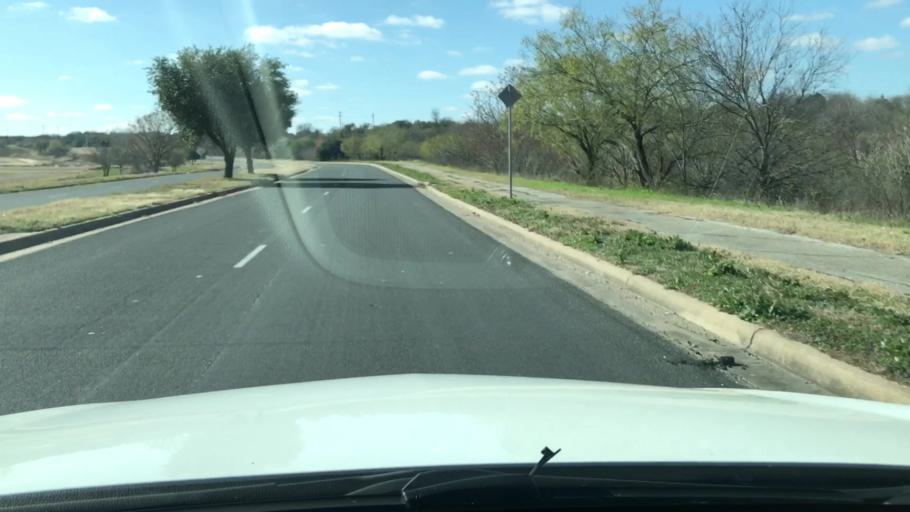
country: US
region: Texas
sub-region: Travis County
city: Onion Creek
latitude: 30.1836
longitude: -97.7185
